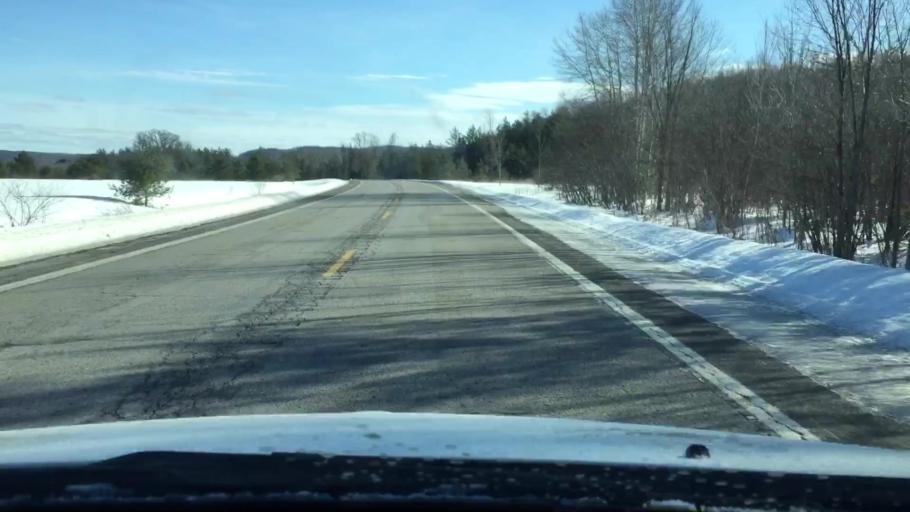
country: US
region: Michigan
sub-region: Charlevoix County
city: East Jordan
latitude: 45.1075
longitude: -85.1261
